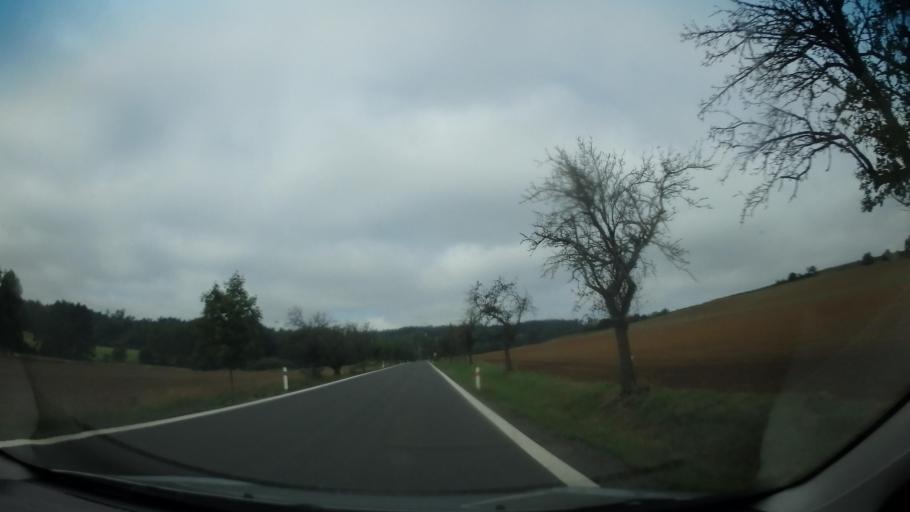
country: CZ
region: Central Bohemia
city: Neveklov
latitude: 49.7537
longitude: 14.5809
